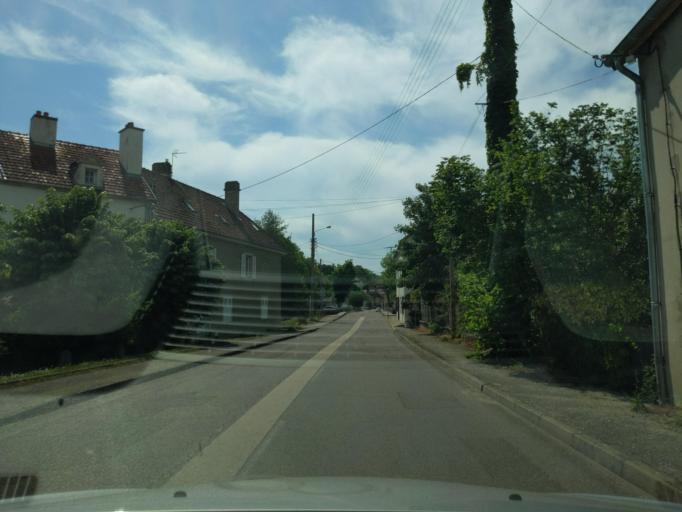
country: FR
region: Bourgogne
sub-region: Departement de la Cote-d'Or
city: Fleurey-sur-Ouche
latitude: 47.2969
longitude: 4.8146
